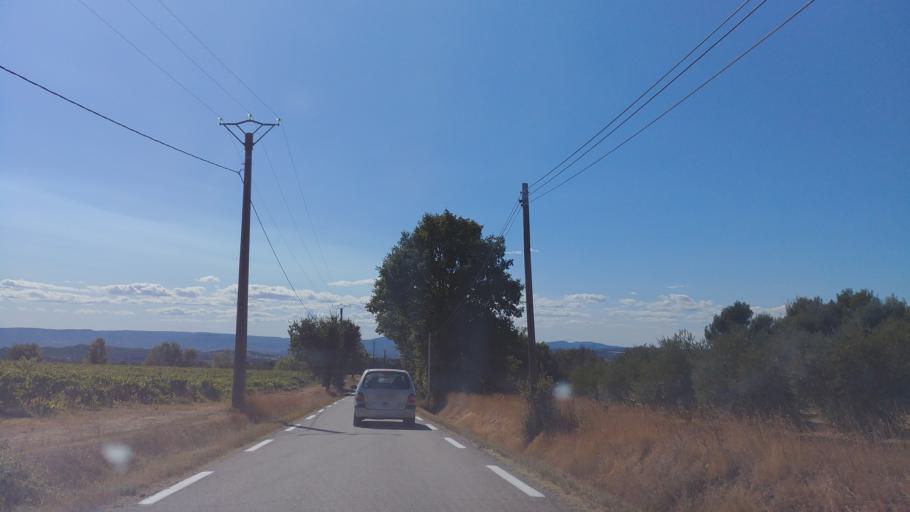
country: FR
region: Provence-Alpes-Cote d'Azur
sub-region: Departement du Vaucluse
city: Grambois
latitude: 43.7258
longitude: 5.5948
